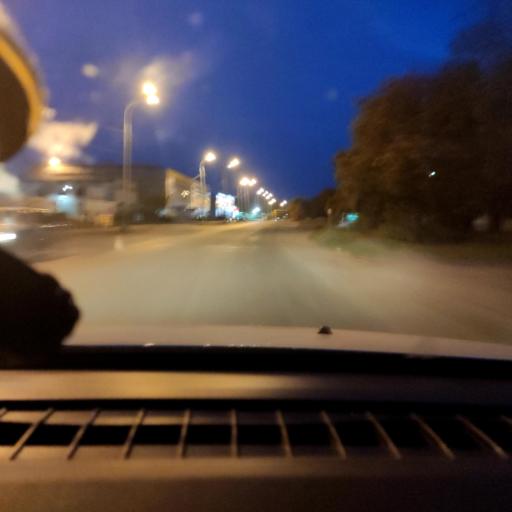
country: RU
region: Samara
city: Samara
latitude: 53.1340
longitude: 50.1202
